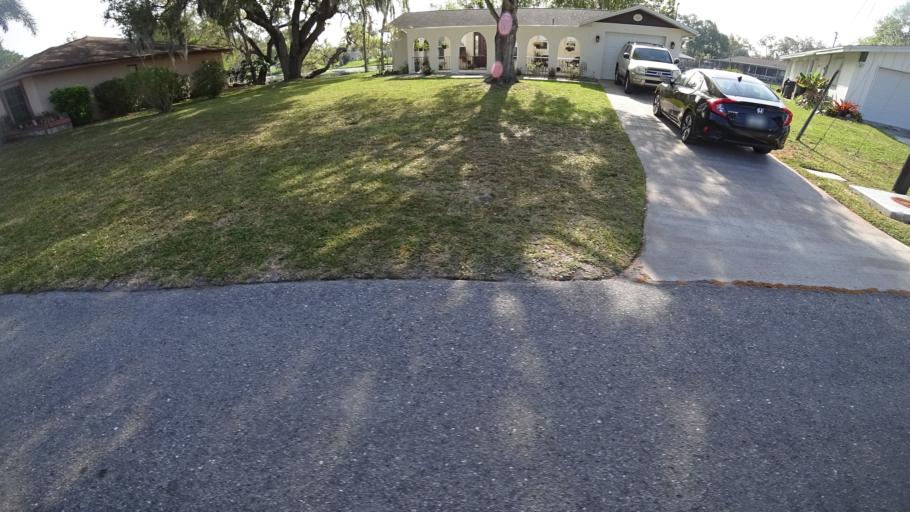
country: US
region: Florida
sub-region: Manatee County
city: Whitfield
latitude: 27.4238
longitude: -82.5500
